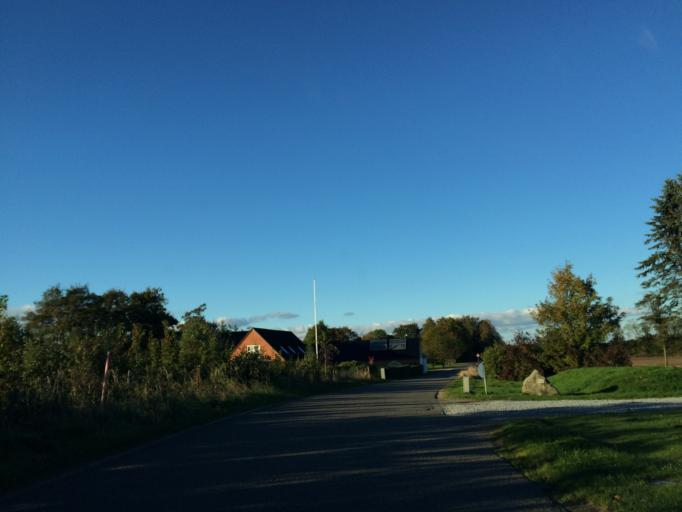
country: DK
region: Central Jutland
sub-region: Silkeborg Kommune
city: Svejbaek
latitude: 56.1680
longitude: 9.6932
